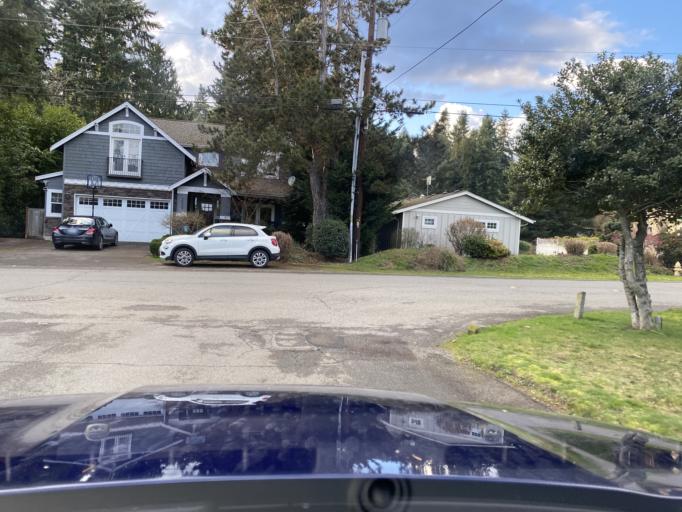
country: US
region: Washington
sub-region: King County
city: Newport
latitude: 47.5853
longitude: -122.1937
